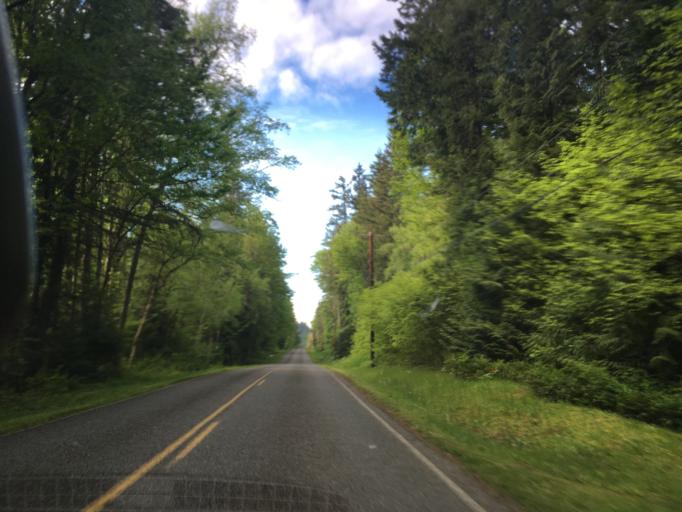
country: US
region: Washington
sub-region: Whatcom County
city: Sudden Valley
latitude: 48.7649
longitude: -122.3553
